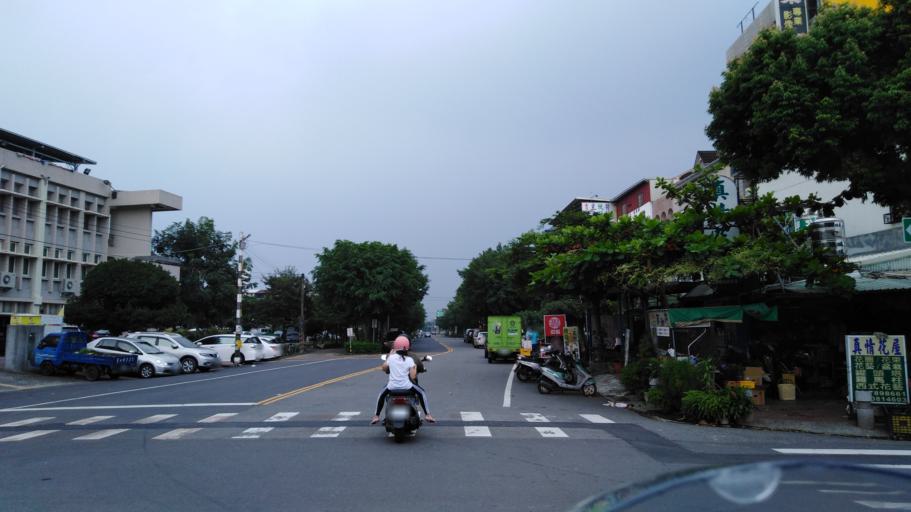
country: TW
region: Taiwan
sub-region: Pingtung
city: Pingtung
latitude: 22.5497
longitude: 120.5427
